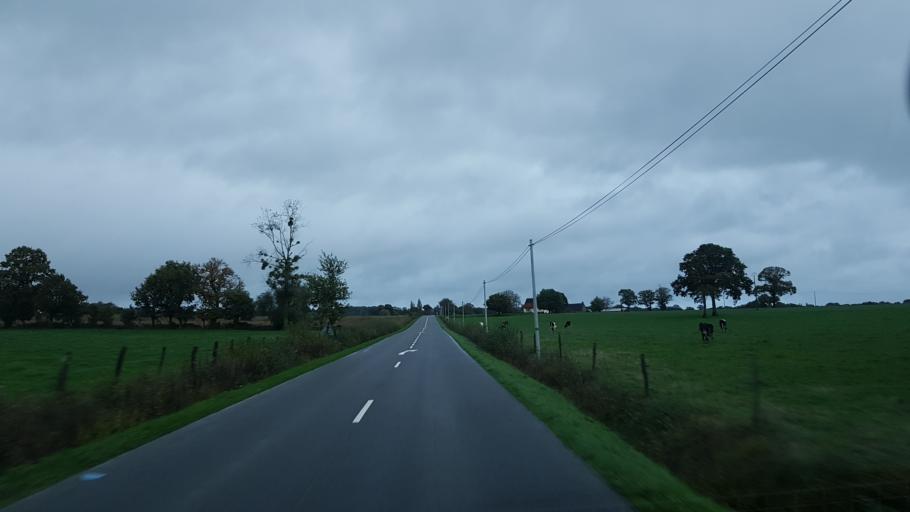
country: FR
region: Pays de la Loire
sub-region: Departement de la Mayenne
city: Juvigne
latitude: 48.1902
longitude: -1.0919
